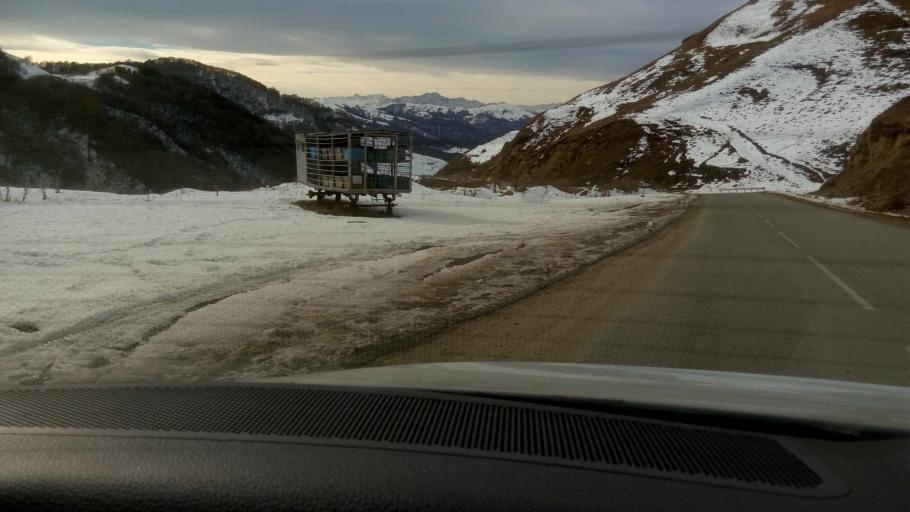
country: RU
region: Karachayevo-Cherkesiya
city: Karachayevsk
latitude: 43.7802
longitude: 42.1779
